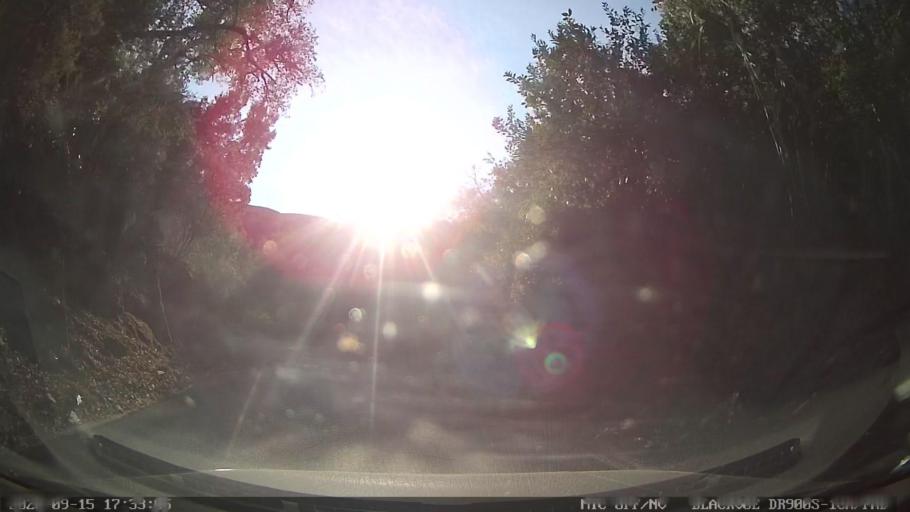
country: PT
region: Vila Real
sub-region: Sabrosa
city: Vilela
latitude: 41.2128
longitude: -7.5786
